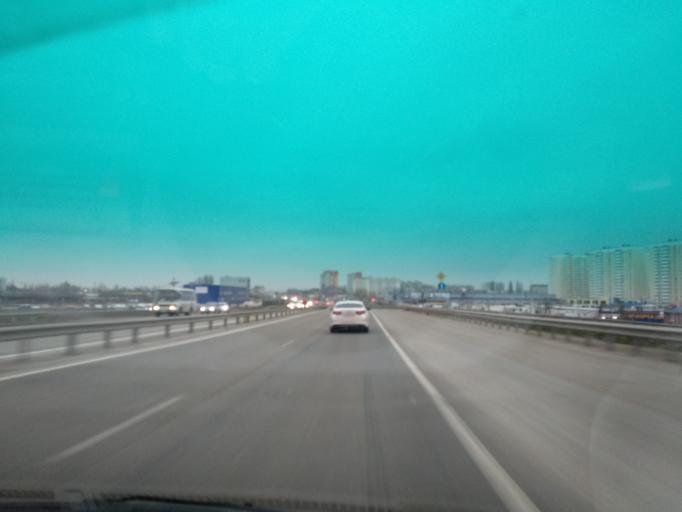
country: RU
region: Krasnodarskiy
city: Pashkovskiy
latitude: 45.0419
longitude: 39.1282
